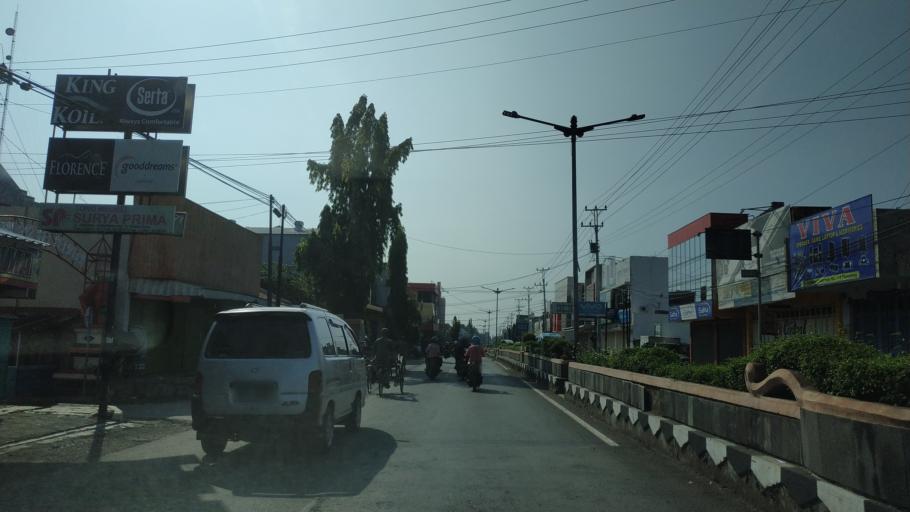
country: ID
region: Central Java
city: Pemalang
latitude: -6.8903
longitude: 109.3887
